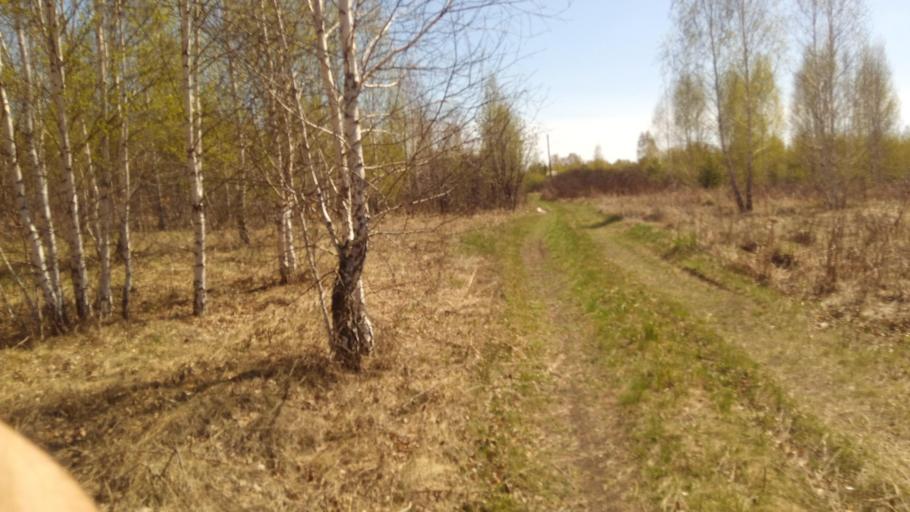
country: RU
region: Chelyabinsk
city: Timiryazevskiy
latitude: 54.9974
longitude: 60.8510
